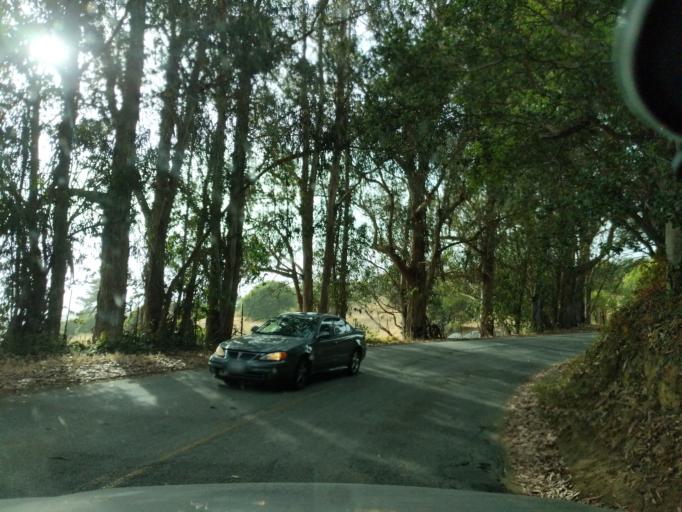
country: US
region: California
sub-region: Monterey County
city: Elkhorn
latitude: 36.8255
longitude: -121.7320
